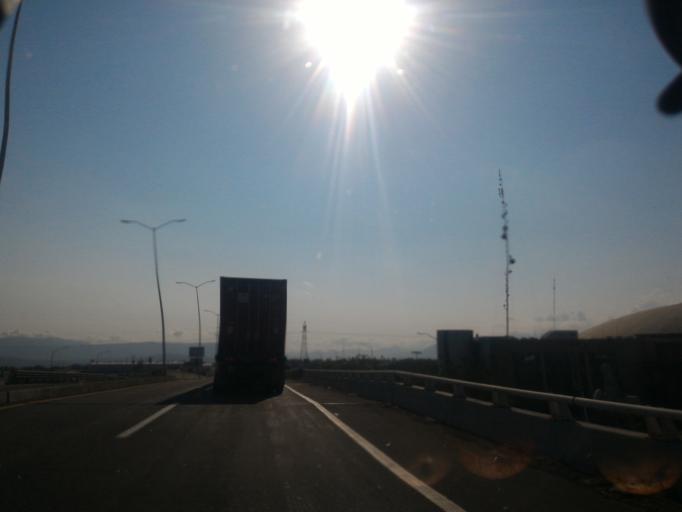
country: MX
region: Colima
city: Colima
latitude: 19.2555
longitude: -103.6868
